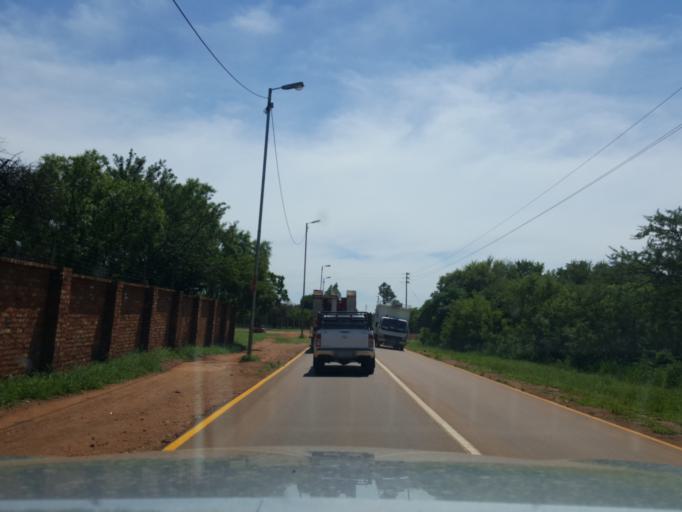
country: ZA
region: Gauteng
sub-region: City of Tshwane Metropolitan Municipality
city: Pretoria
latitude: -25.6732
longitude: 28.3034
